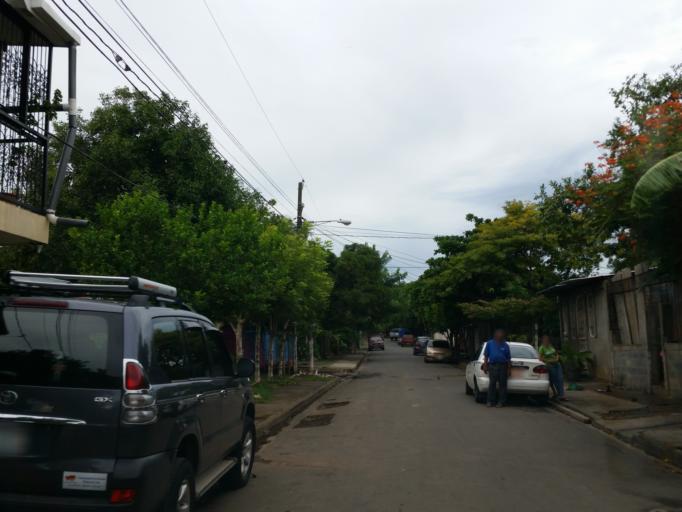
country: NI
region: Managua
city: Managua
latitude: 12.1231
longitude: -86.2734
